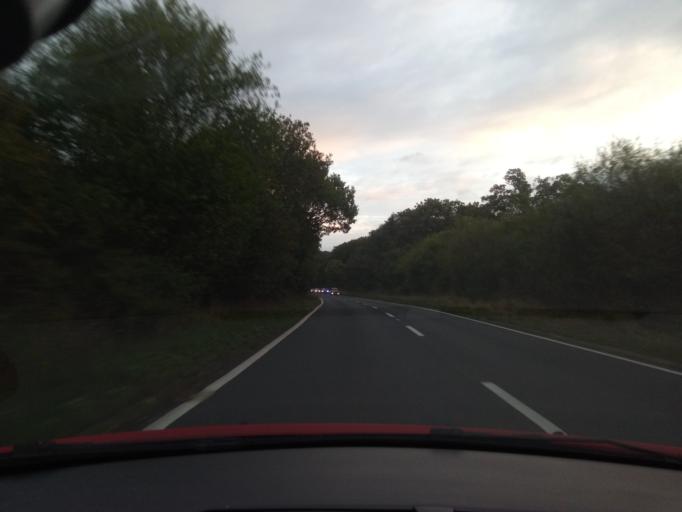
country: GB
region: England
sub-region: Essex
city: Rowhedge
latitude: 51.8428
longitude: 0.9153
